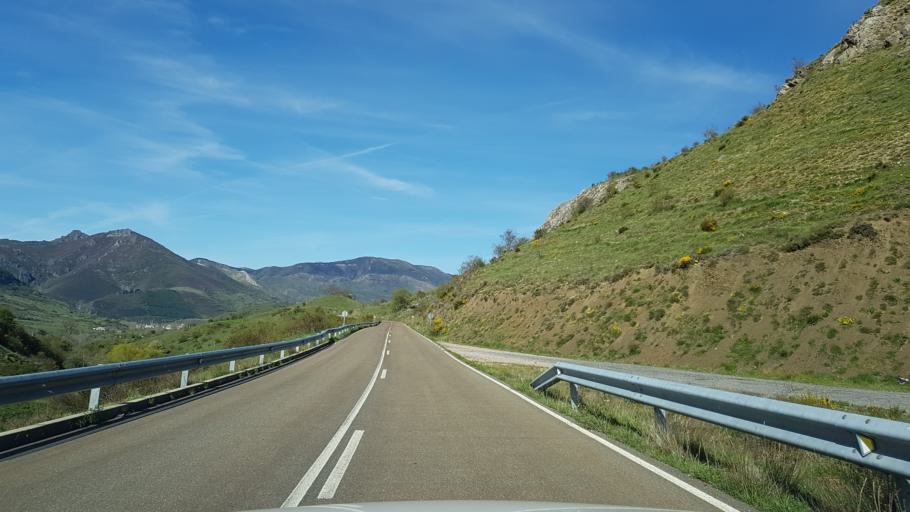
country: ES
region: Castille and Leon
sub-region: Provincia de Leon
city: Villamanin
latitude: 42.9519
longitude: -5.6276
